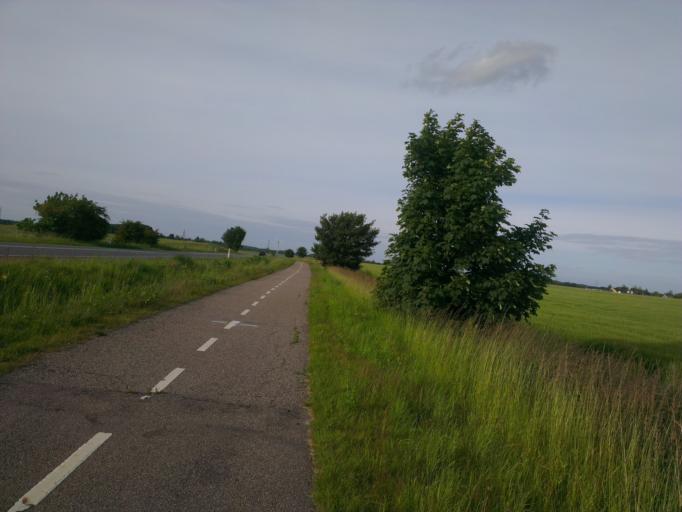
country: DK
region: Capital Region
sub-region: Frederikssund Kommune
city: Skibby
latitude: 55.7856
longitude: 11.9738
